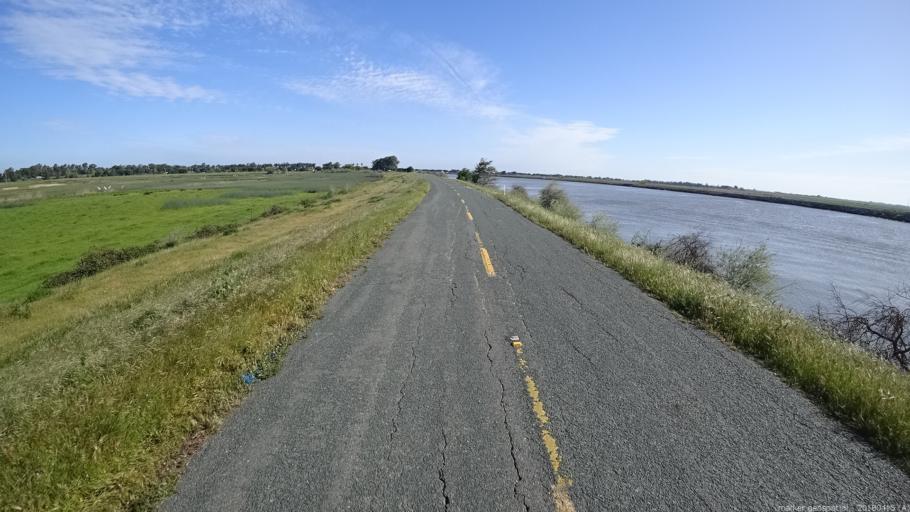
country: US
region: California
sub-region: Solano County
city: Rio Vista
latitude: 38.1071
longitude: -121.6852
